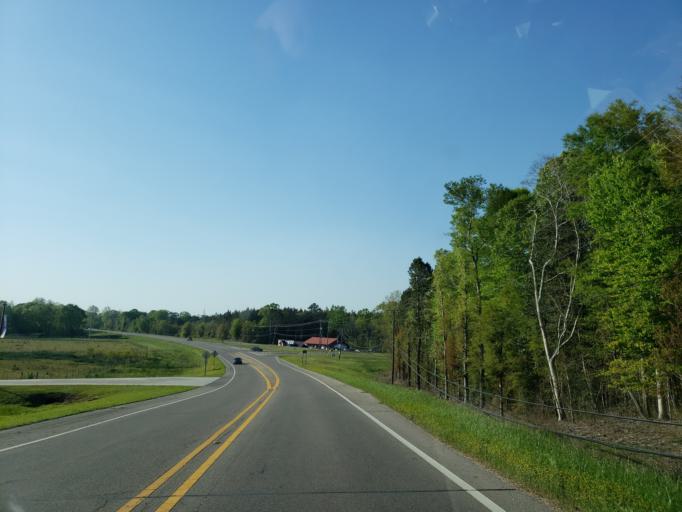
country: US
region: Mississippi
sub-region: Jones County
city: Laurel
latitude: 31.6769
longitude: -89.1099
